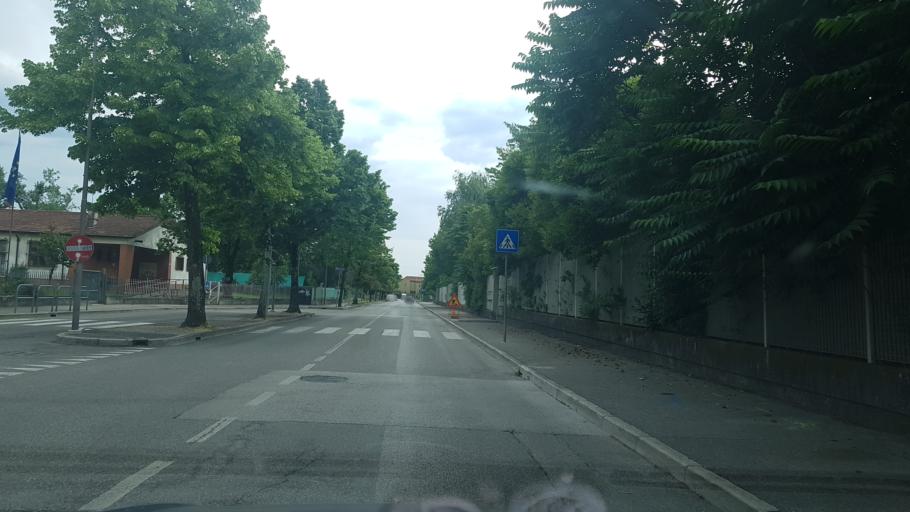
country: IT
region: Friuli Venezia Giulia
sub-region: Provincia di Gorizia
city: Gorizia
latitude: 45.9314
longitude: 13.6172
